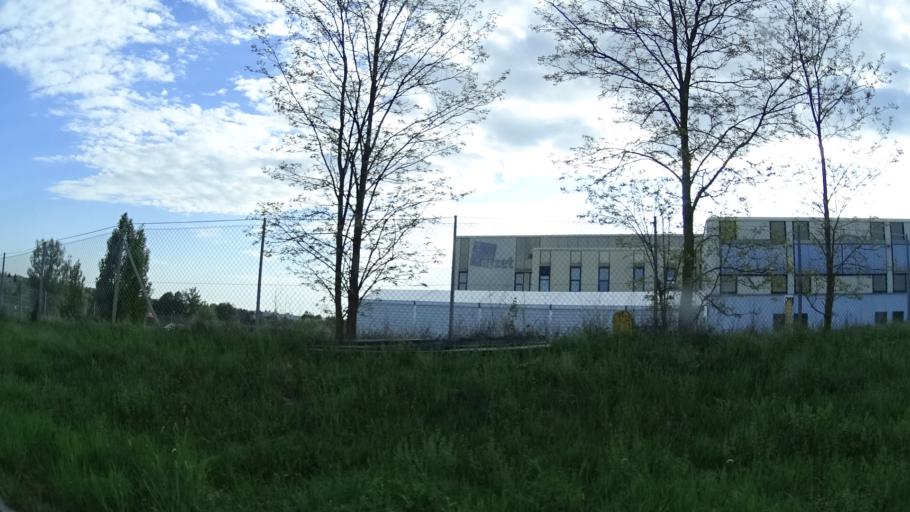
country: DE
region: Baden-Wuerttemberg
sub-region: Tuebingen Region
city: Haigerloch
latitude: 48.3657
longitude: 8.7780
